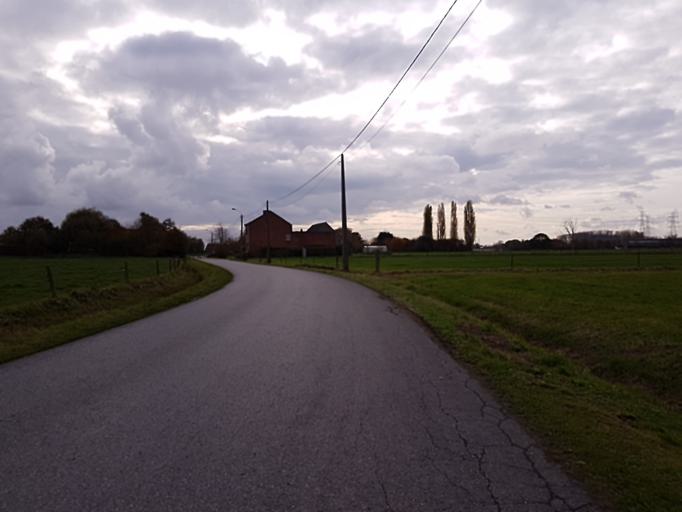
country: BE
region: Flanders
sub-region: Provincie Antwerpen
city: Lint
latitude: 51.1211
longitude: 4.5264
